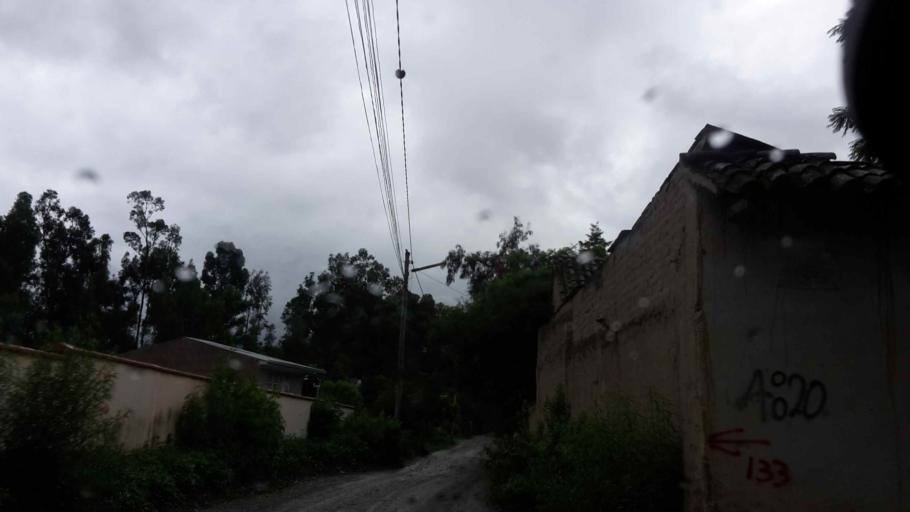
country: BO
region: Cochabamba
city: Cochabamba
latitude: -17.3585
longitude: -66.2167
